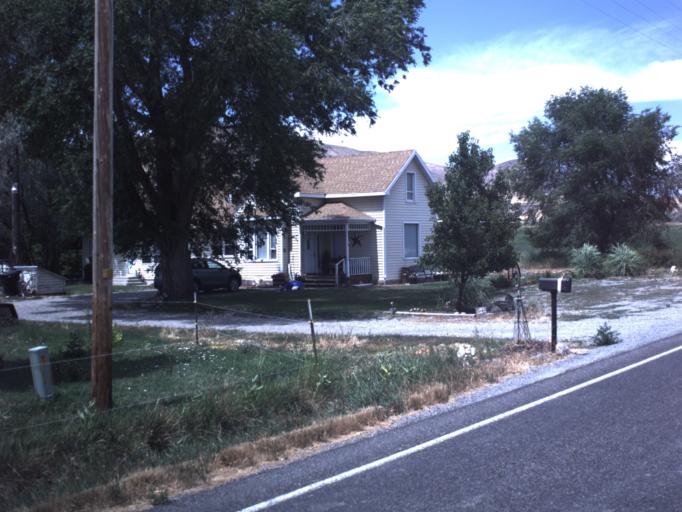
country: US
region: Utah
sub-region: Box Elder County
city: Tremonton
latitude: 41.6541
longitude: -112.2958
